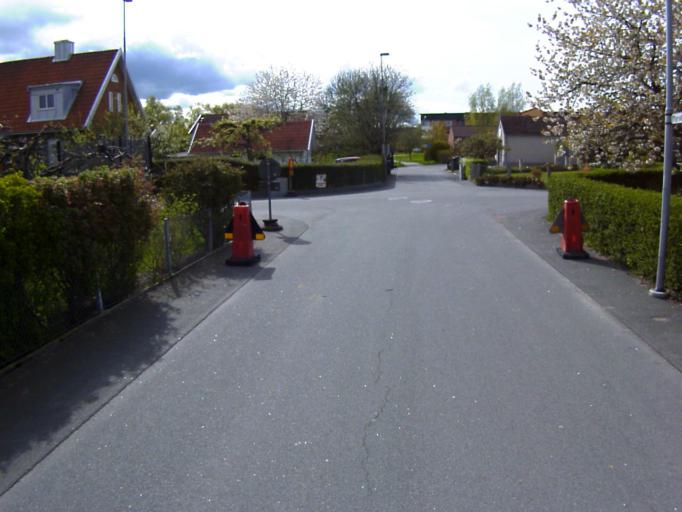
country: SE
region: Skane
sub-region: Kristianstads Kommun
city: Kristianstad
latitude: 56.0468
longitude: 14.1698
